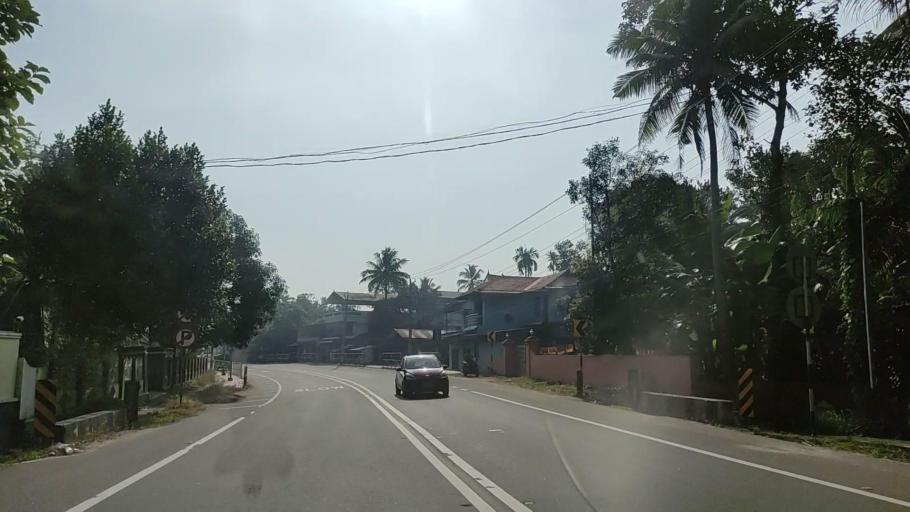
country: IN
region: Kerala
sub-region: Kollam
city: Punalur
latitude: 8.9760
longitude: 76.8167
